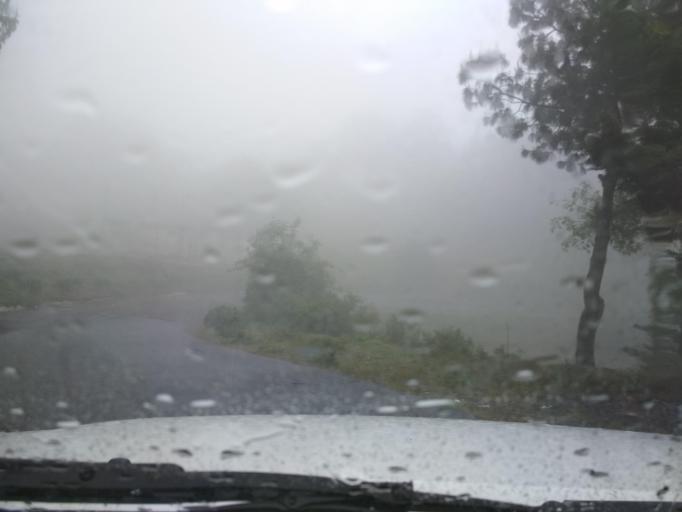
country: MX
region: Veracruz
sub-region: Mariano Escobedo
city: San Isidro el Berro
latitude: 18.9307
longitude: -97.2119
